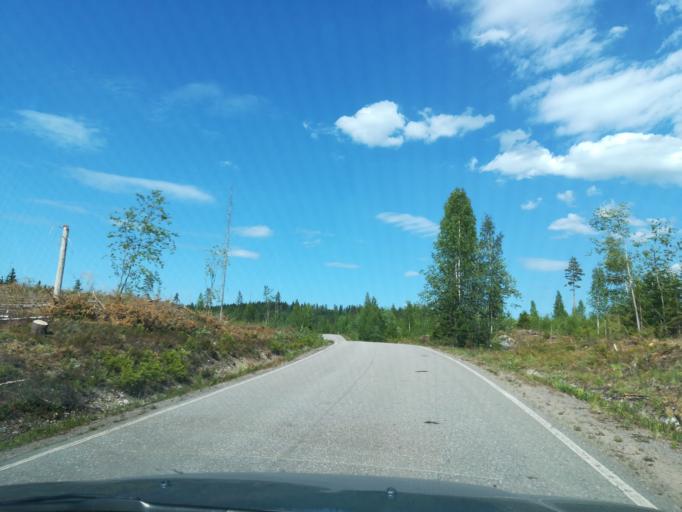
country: FI
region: South Karelia
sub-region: Imatra
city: Ruokolahti
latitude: 61.4754
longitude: 28.8711
